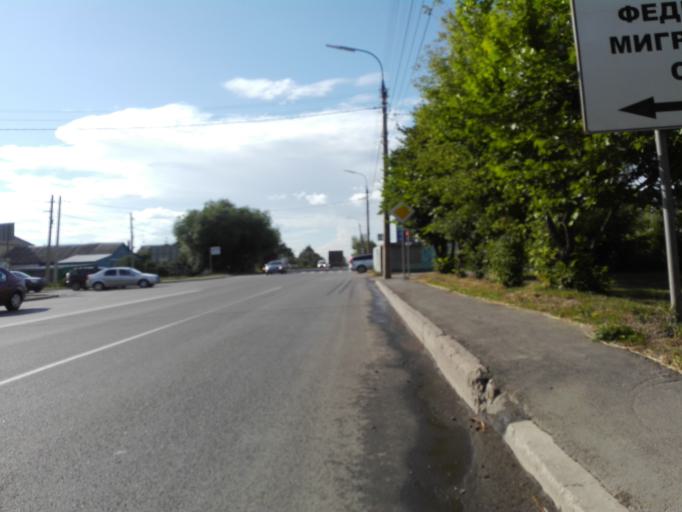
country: RU
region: Orjol
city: Orel
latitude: 52.9925
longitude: 36.1157
